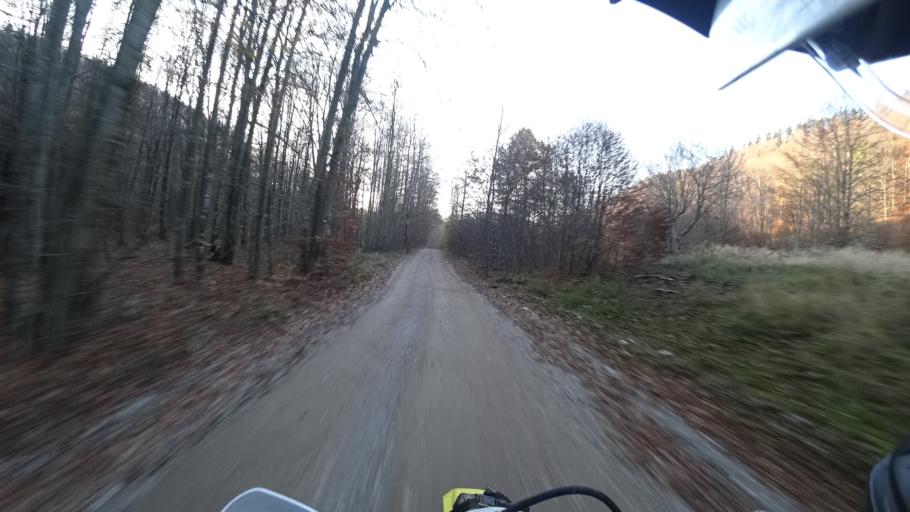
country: HR
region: Primorsko-Goranska
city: Klana
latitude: 45.5015
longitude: 14.4425
